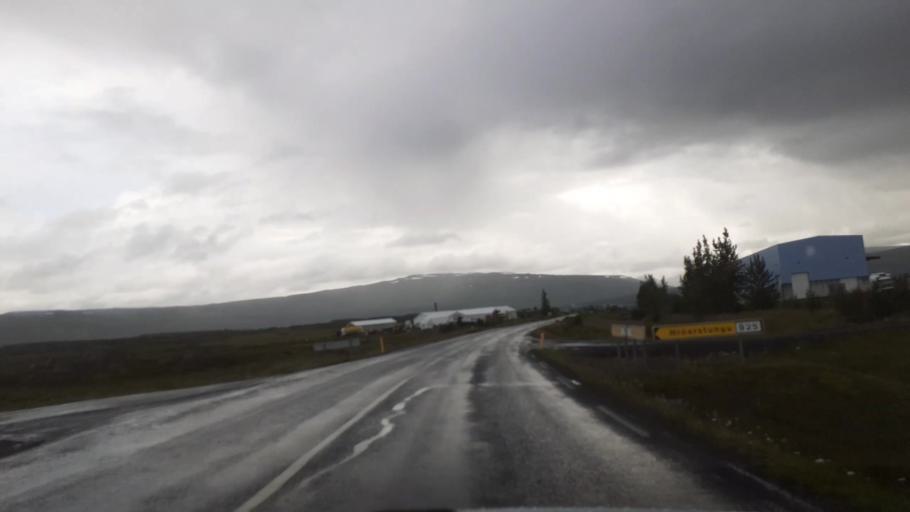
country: IS
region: East
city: Egilsstadir
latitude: 65.2984
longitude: -14.4472
